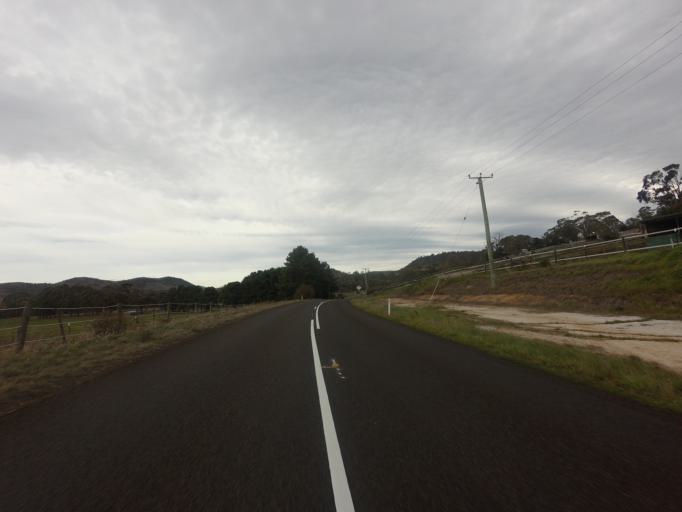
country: AU
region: Tasmania
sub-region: Brighton
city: Bridgewater
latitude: -42.6724
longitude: 147.1519
